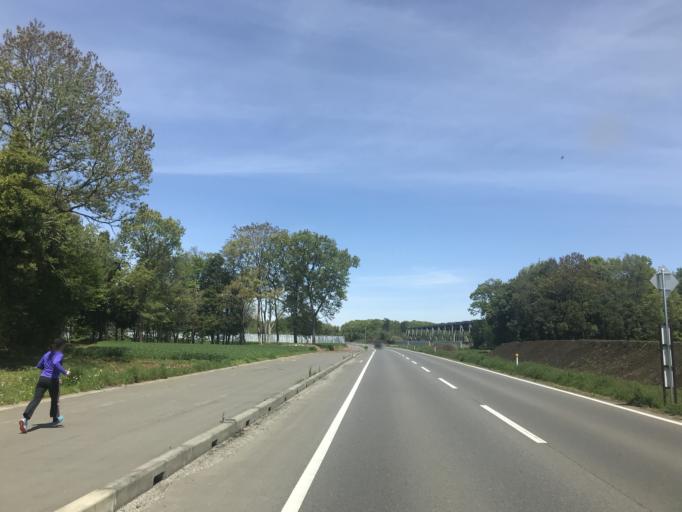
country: JP
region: Ibaraki
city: Shimodate
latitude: 36.2938
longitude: 140.0131
